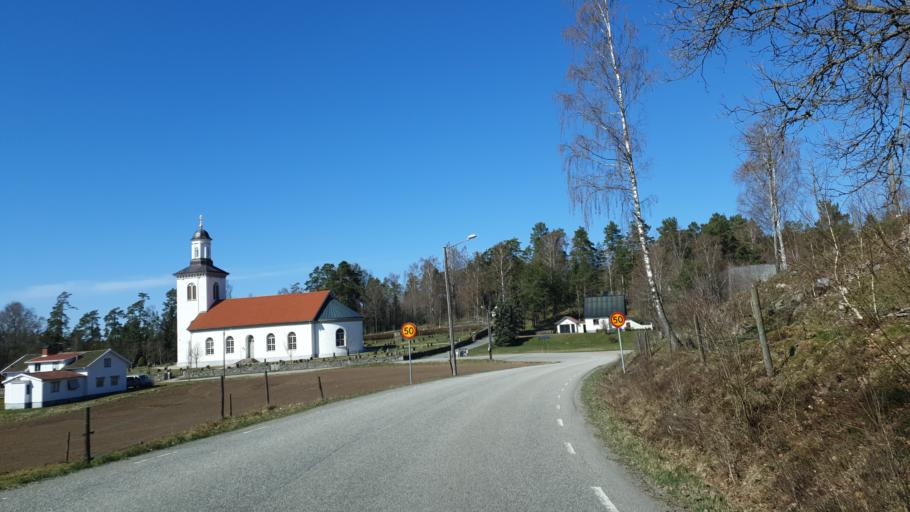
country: SE
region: Vaestra Goetaland
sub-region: Svenljunga Kommun
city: Svenljunga
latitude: 57.4412
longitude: 13.1243
